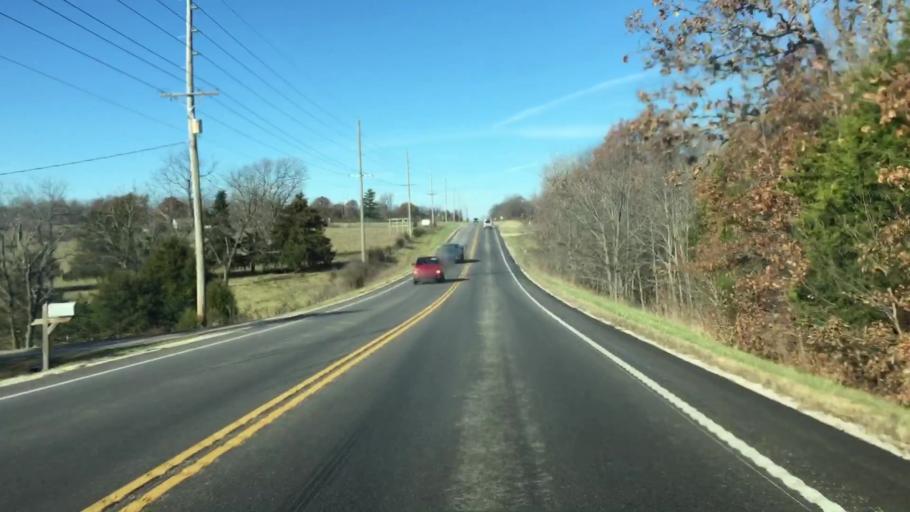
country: US
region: Missouri
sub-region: Miller County
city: Eldon
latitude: 38.3764
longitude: -92.6617
